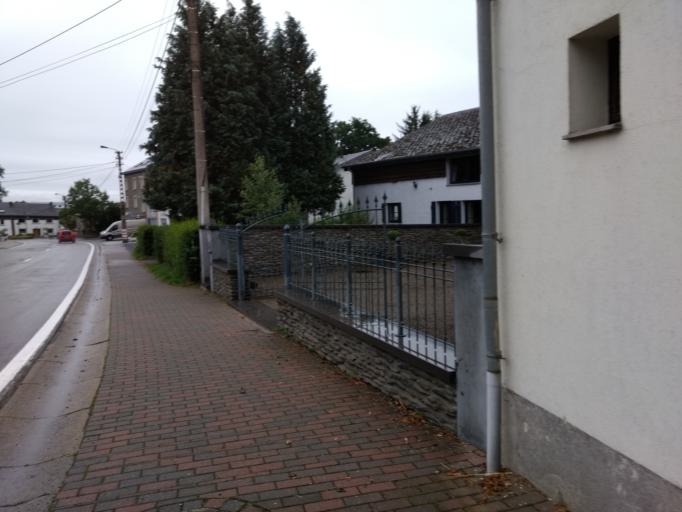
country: BE
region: Wallonia
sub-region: Province du Luxembourg
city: Bertogne
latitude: 50.1602
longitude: 5.6815
